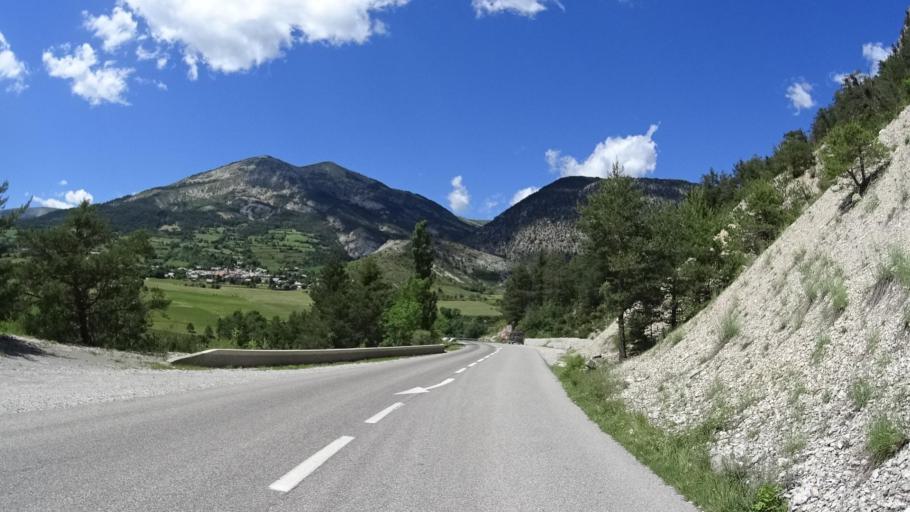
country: FR
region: Provence-Alpes-Cote d'Azur
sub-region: Departement des Alpes-de-Haute-Provence
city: Annot
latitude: 44.0908
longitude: 6.5661
